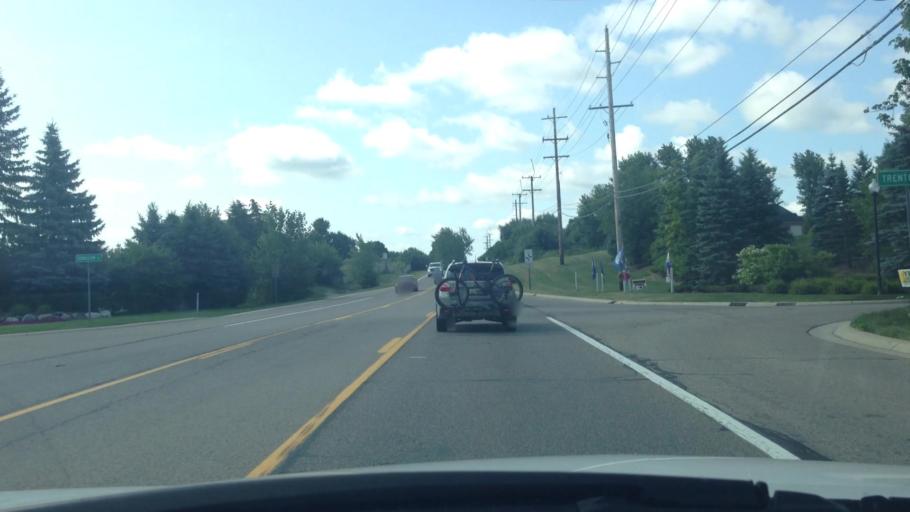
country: US
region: Michigan
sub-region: Oakland County
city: Waterford
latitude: 42.6314
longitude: -83.4427
